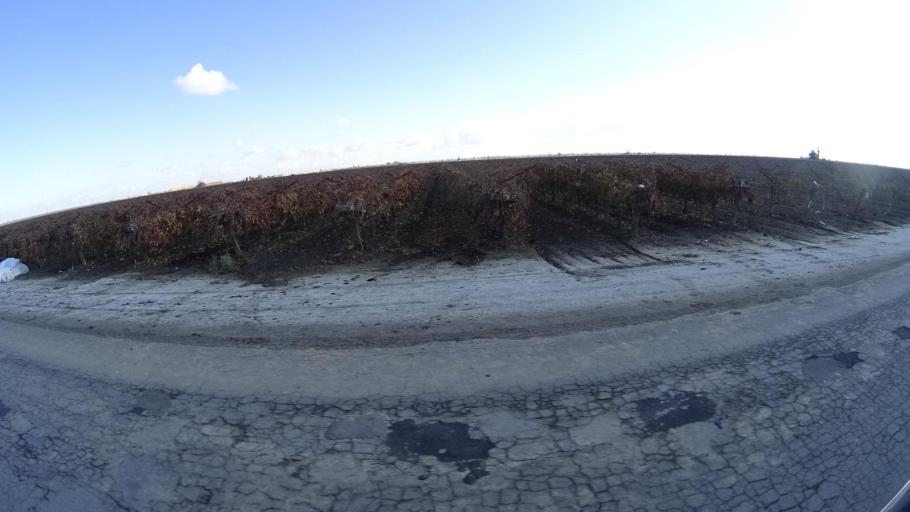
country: US
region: California
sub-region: Kern County
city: McFarland
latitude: 35.6854
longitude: -119.2587
